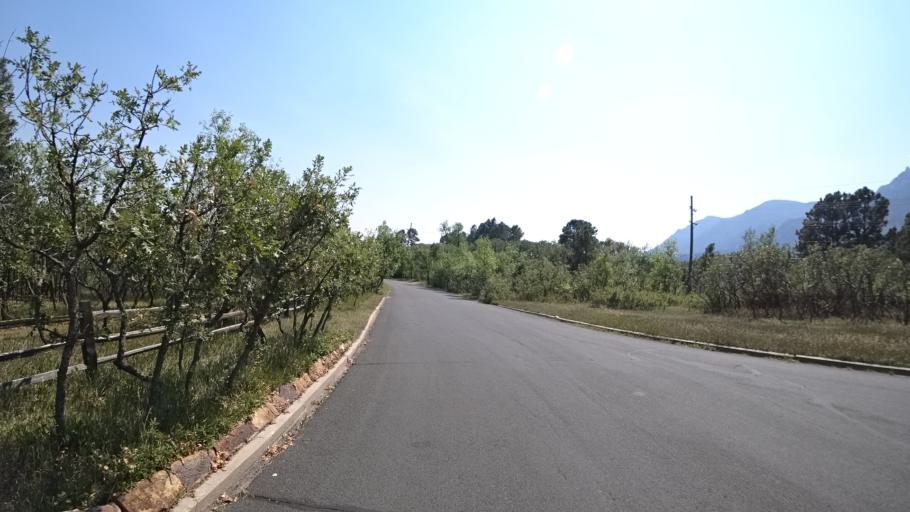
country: US
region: Colorado
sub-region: El Paso County
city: Colorado Springs
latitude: 38.7822
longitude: -104.8441
